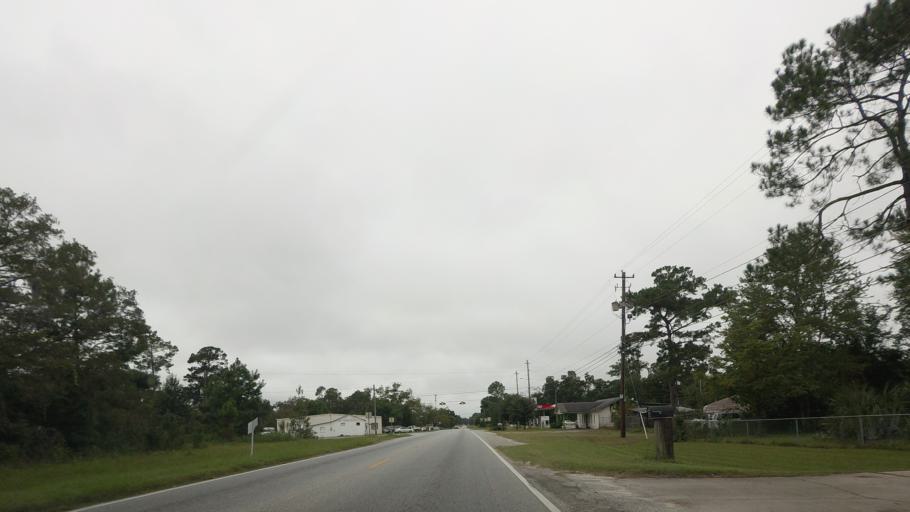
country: US
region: Georgia
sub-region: Lowndes County
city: Valdosta
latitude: 30.8175
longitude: -83.2595
